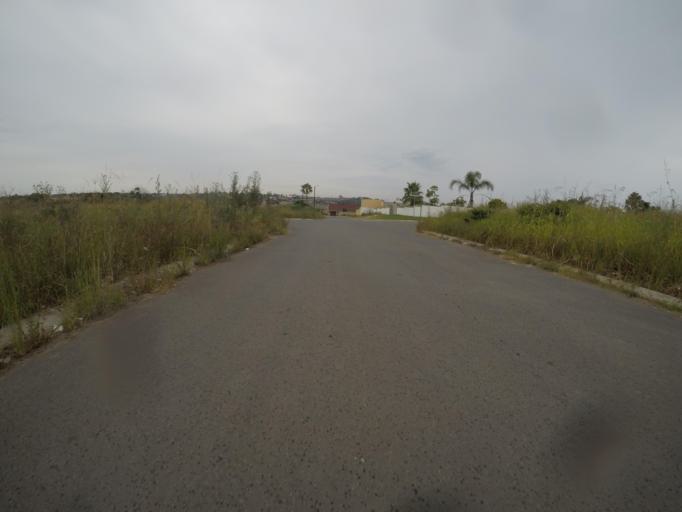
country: ZA
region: Eastern Cape
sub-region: Buffalo City Metropolitan Municipality
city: East London
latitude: -33.0027
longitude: 27.8526
